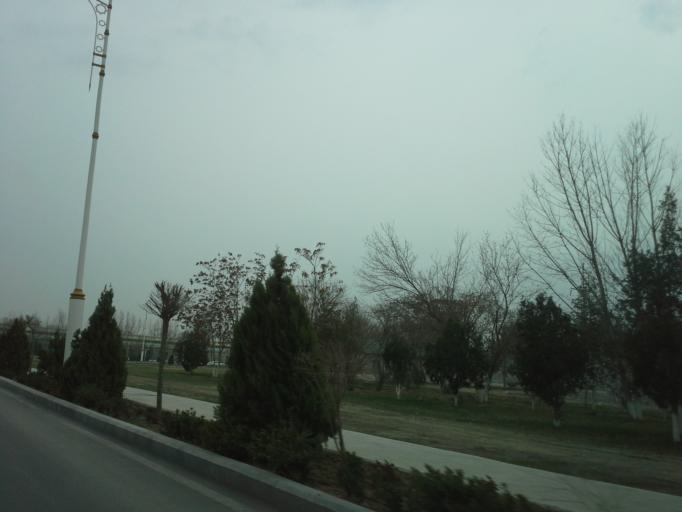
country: TM
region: Ahal
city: Ashgabat
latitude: 37.9634
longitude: 58.3609
